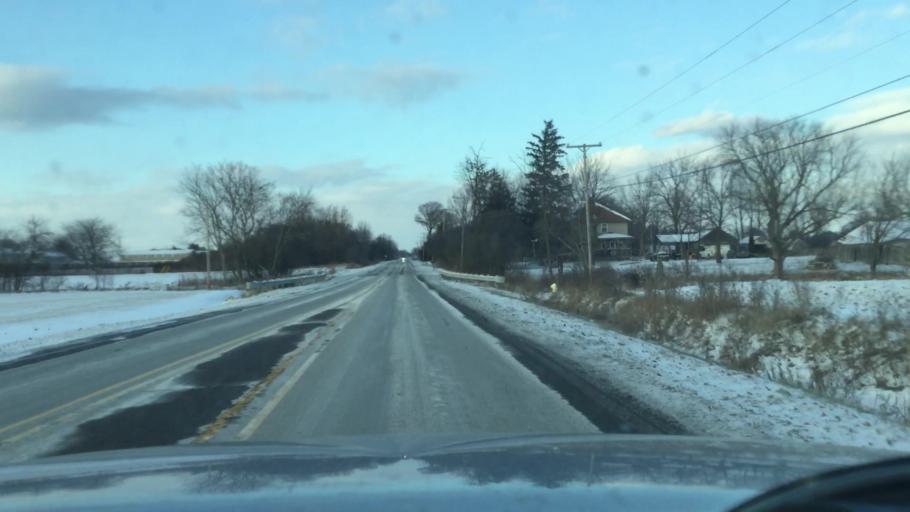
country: US
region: Michigan
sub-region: Saginaw County
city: Saginaw
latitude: 43.3778
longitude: -83.9354
